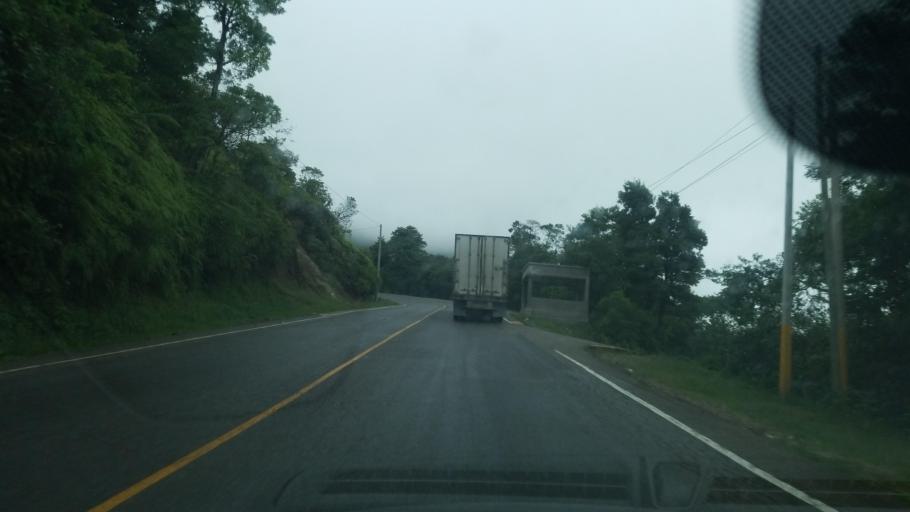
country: HN
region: Ocotepeque
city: La Labor
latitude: 14.4682
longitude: -89.0686
